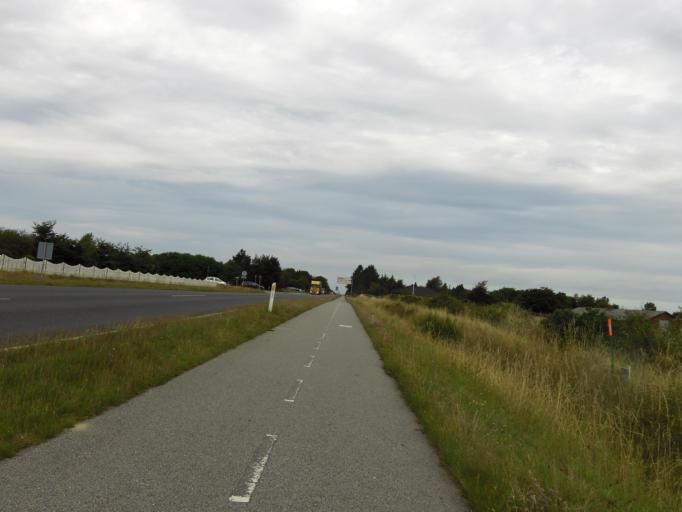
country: DK
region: South Denmark
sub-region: Esbjerg Kommune
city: Ribe
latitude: 55.3131
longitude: 8.7935
